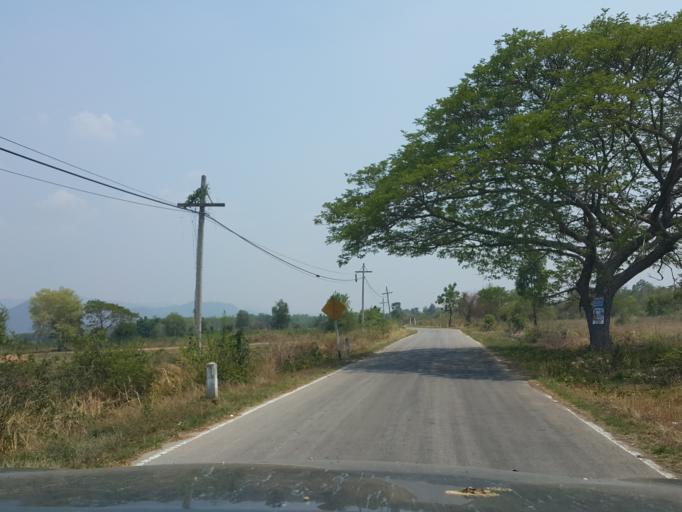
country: TH
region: Lampang
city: Mae Phrik
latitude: 17.5244
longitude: 99.1477
